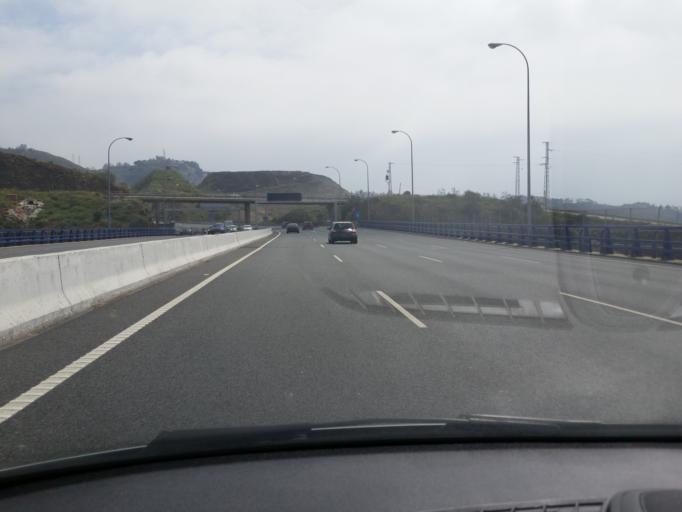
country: ES
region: Andalusia
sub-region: Provincia de Malaga
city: Malaga
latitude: 36.7412
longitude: -4.4021
